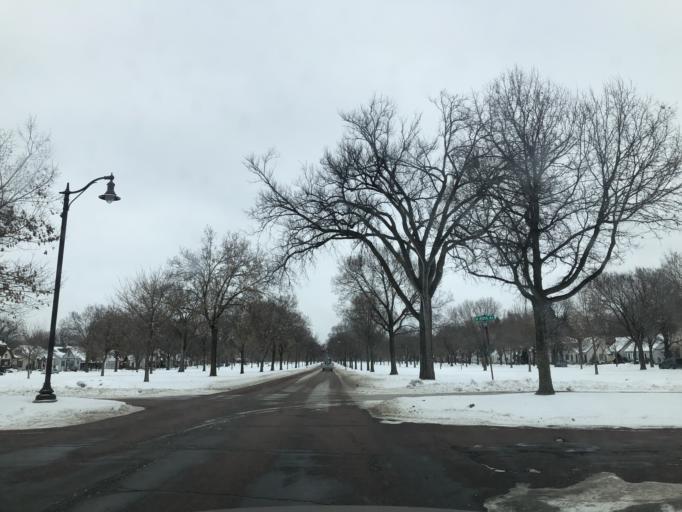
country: US
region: Minnesota
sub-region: Hennepin County
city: Robbinsdale
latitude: 45.0276
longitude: -93.3192
